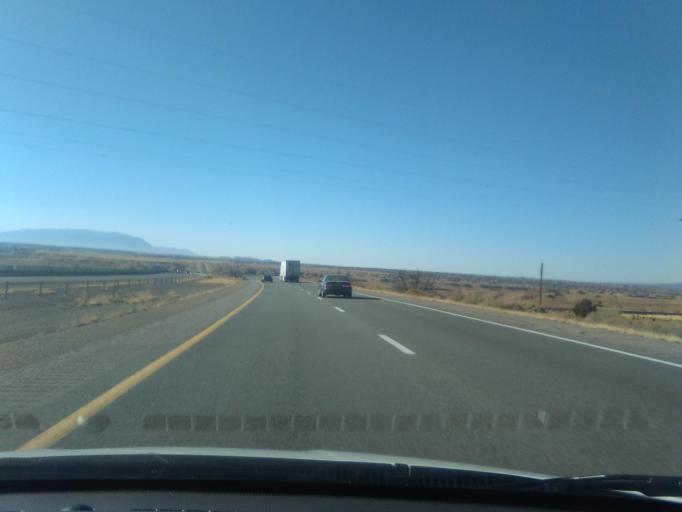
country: US
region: New Mexico
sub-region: Sandoval County
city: Santo Domingo Pueblo
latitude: 35.5071
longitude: -106.2438
